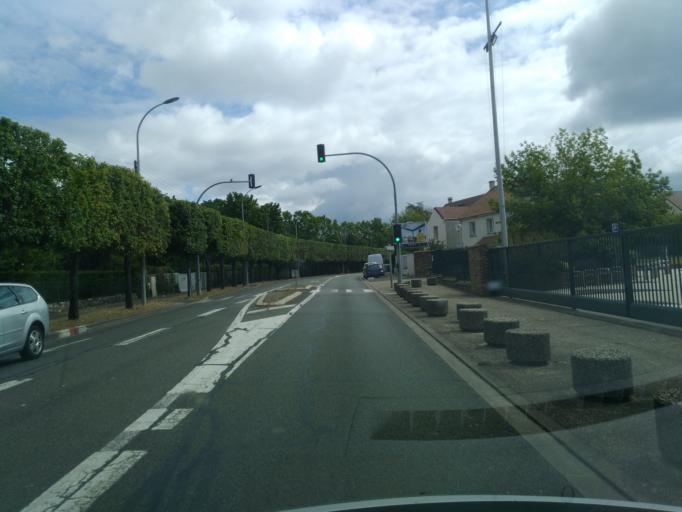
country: FR
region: Ile-de-France
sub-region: Departement des Yvelines
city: Chambourcy
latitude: 48.9186
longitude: 2.0272
